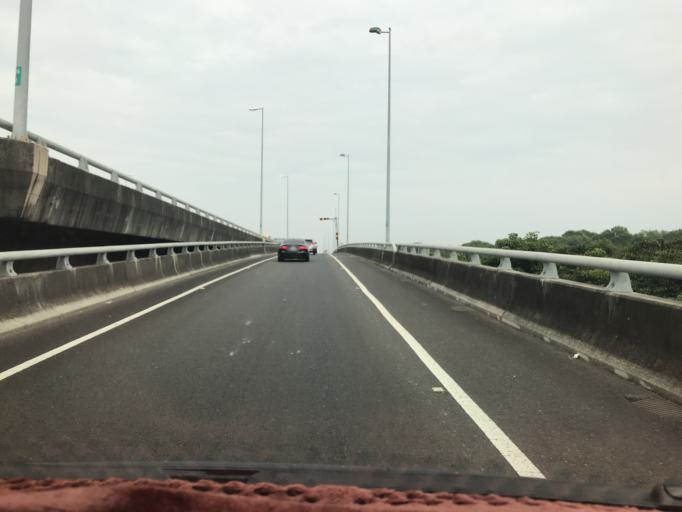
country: TW
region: Taiwan
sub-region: Pingtung
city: Pingtung
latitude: 22.6468
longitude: 120.5430
